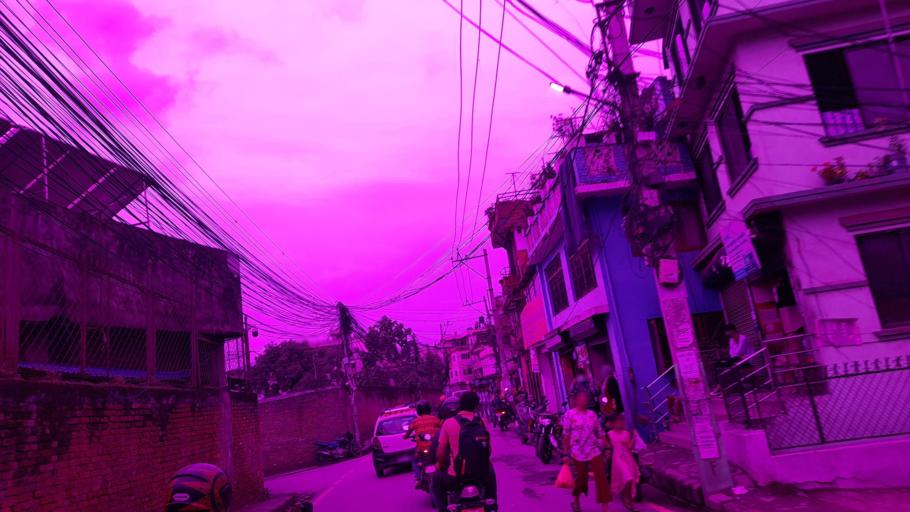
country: NP
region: Central Region
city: Kirtipur
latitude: 27.7015
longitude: 85.2915
